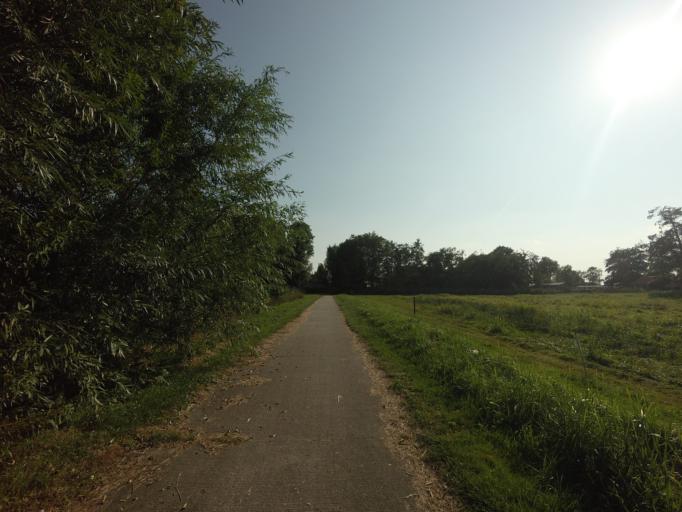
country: NL
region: Groningen
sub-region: Gemeente Zuidhorn
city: Aduard
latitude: 53.1954
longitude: 6.4495
